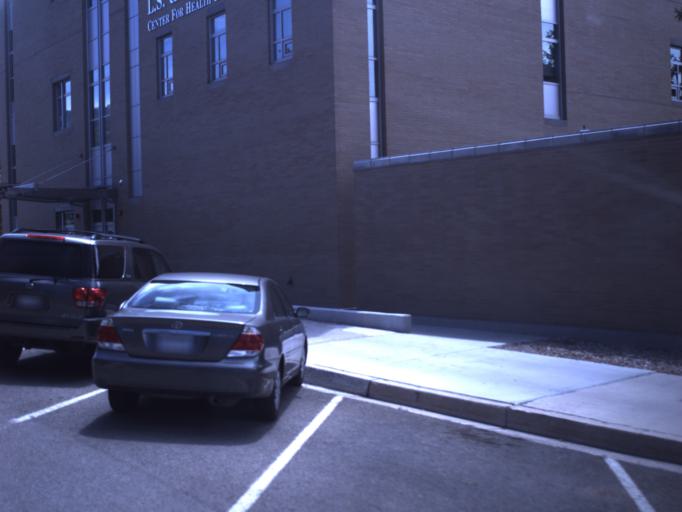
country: US
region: Utah
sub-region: Iron County
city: Cedar City
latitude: 37.6749
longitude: -113.0669
